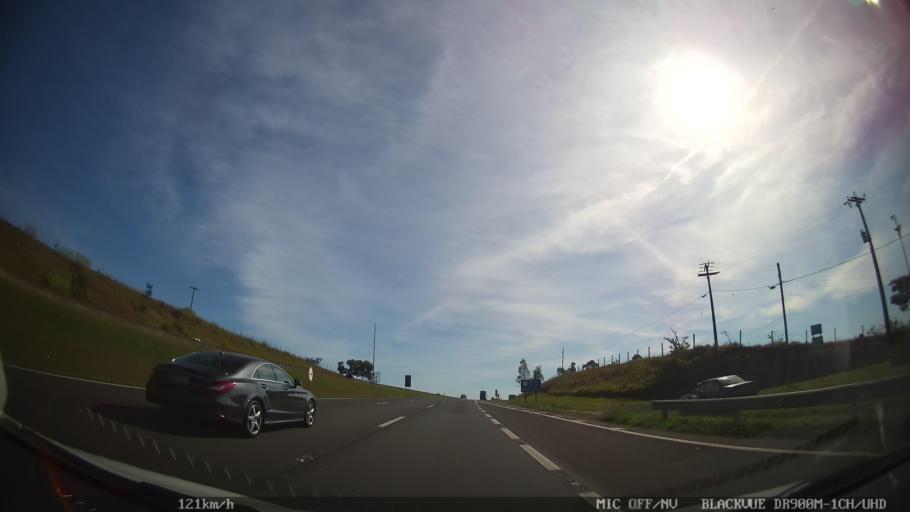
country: BR
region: Sao Paulo
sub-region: Araras
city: Araras
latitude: -22.3883
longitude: -47.3938
